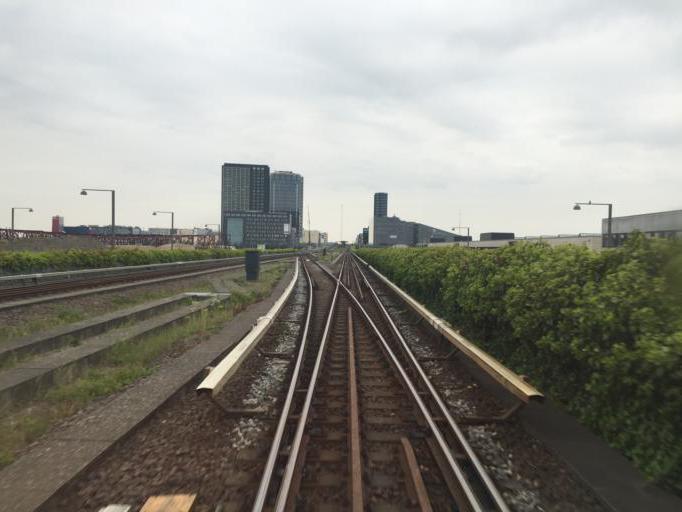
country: DK
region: Capital Region
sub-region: Tarnby Kommune
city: Tarnby
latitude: 55.6218
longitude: 12.5764
